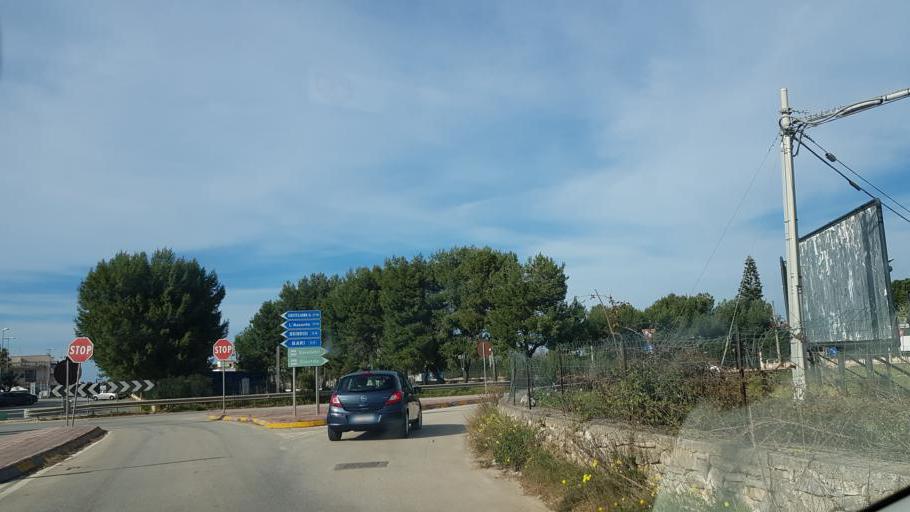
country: IT
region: Apulia
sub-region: Provincia di Brindisi
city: Fasano
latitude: 40.9041
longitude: 17.3500
